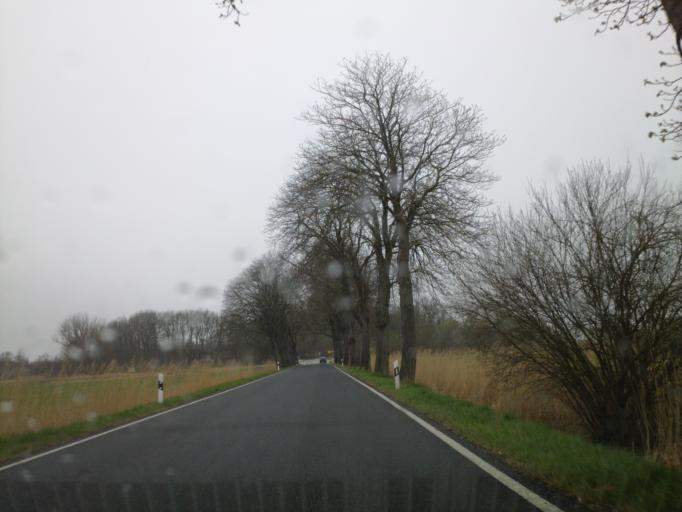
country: DE
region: Mecklenburg-Vorpommern
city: Bad Sulze
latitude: 54.1158
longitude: 12.6694
